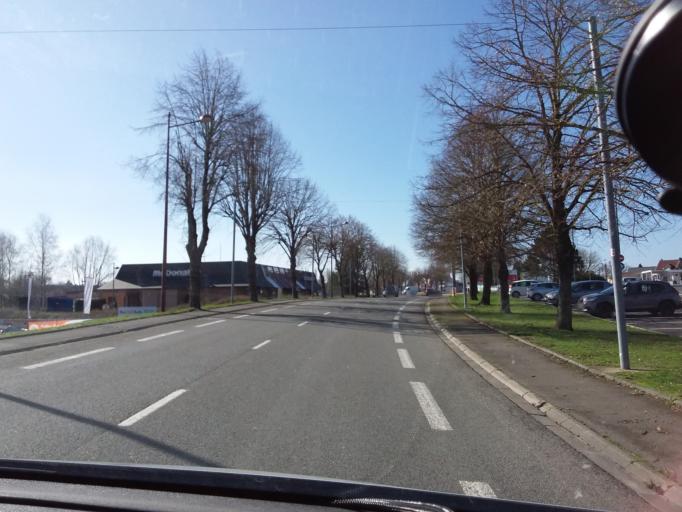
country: FR
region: Picardie
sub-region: Departement de l'Aisne
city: Hirson
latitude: 49.9122
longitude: 4.0919
